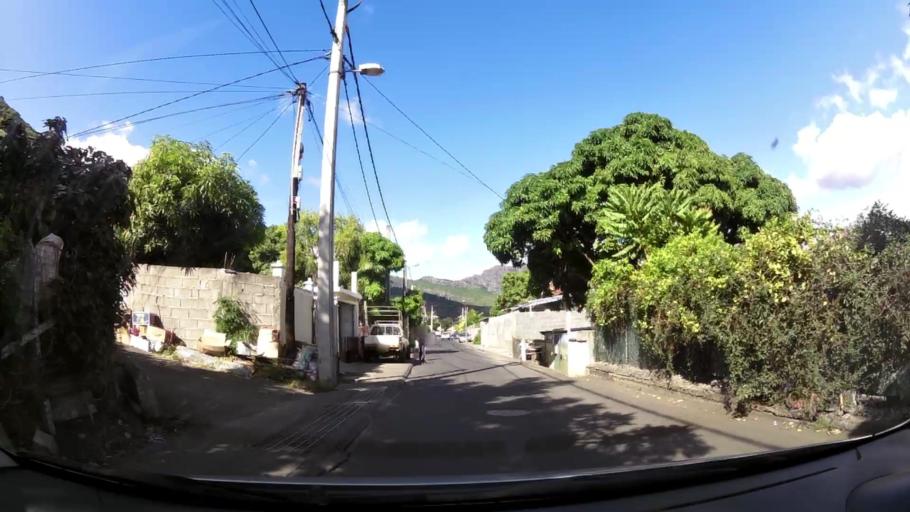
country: MU
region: Port Louis
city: Port Louis
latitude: -20.1612
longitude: 57.5194
